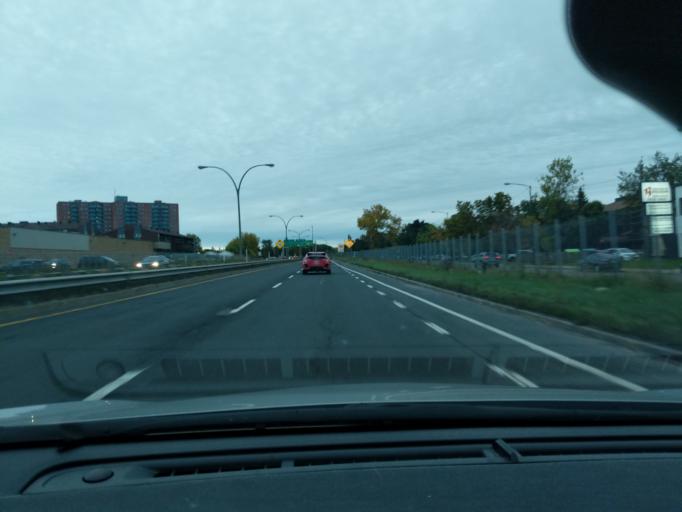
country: CA
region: Quebec
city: L'Ancienne-Lorette
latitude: 46.7639
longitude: -71.3115
